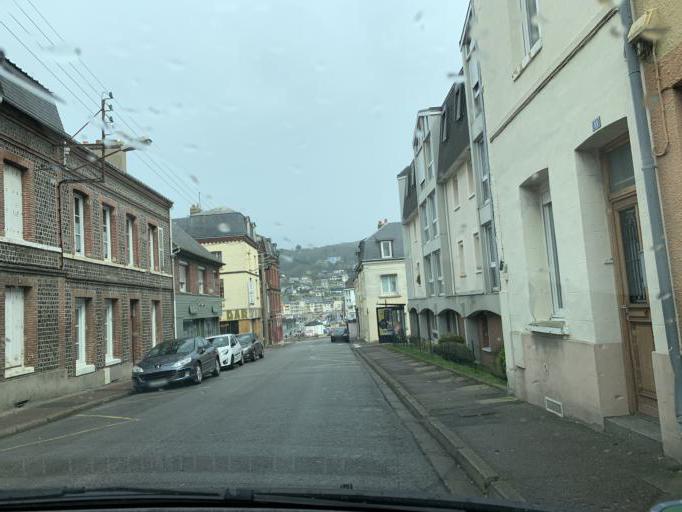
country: FR
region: Haute-Normandie
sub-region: Departement de la Seine-Maritime
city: Fecamp
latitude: 49.7601
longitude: 0.3661
